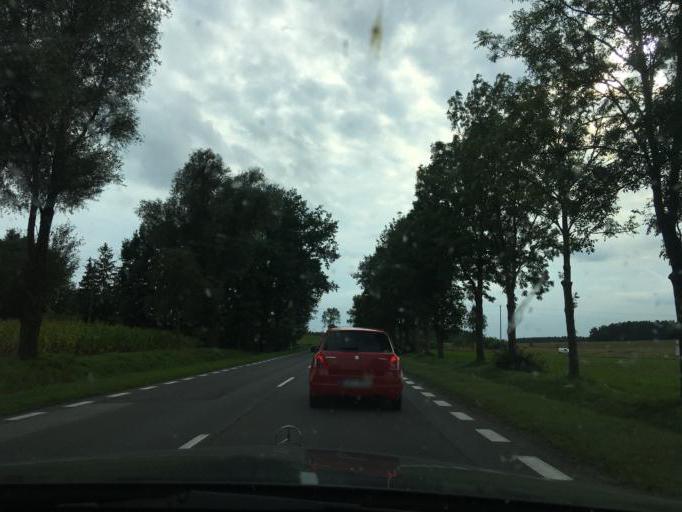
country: PL
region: Podlasie
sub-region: Powiat kolnenski
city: Stawiski
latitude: 53.4549
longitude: 22.1908
